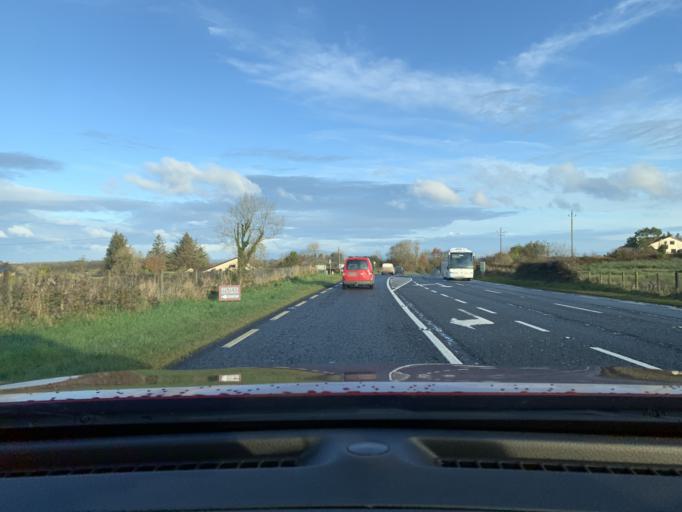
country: IE
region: Connaught
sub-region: Sligo
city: Strandhill
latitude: 54.3689
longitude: -8.5311
